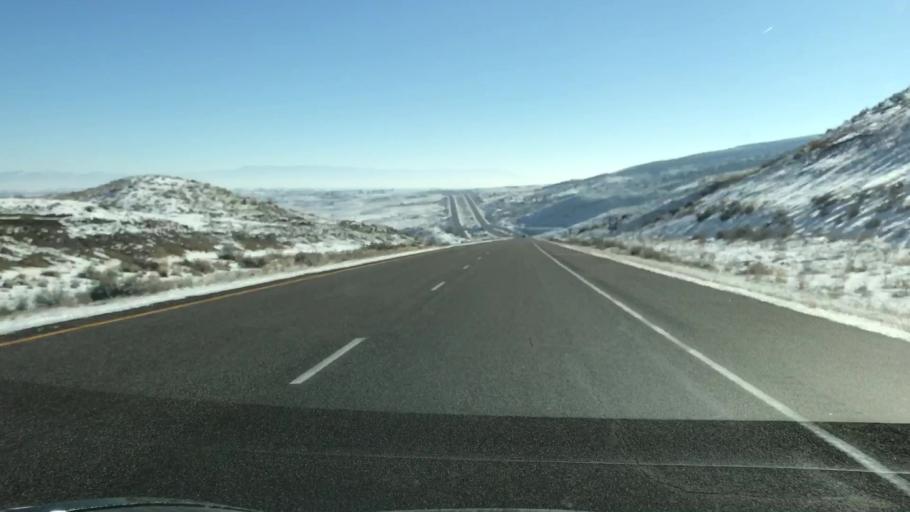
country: US
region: Colorado
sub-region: Mesa County
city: Loma
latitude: 39.2281
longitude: -108.9024
